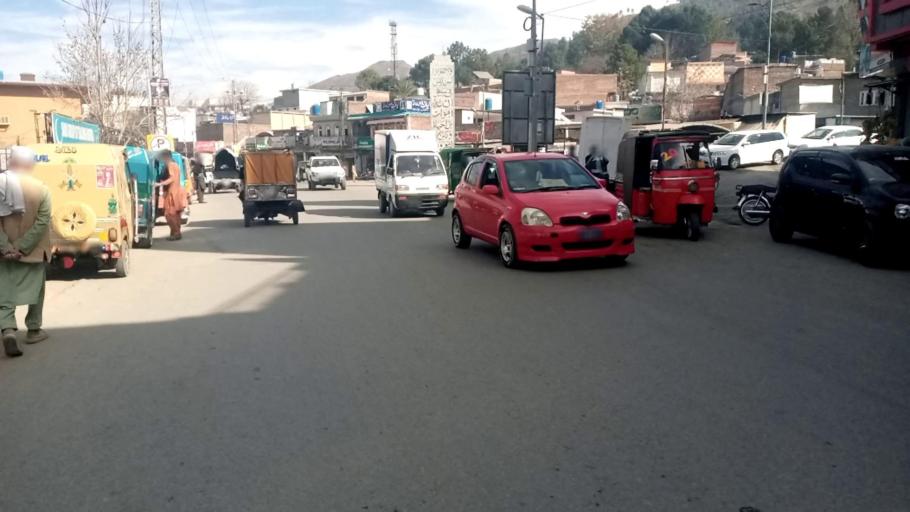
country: PK
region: Khyber Pakhtunkhwa
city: Saidu Sharif
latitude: 34.7491
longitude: 72.3568
